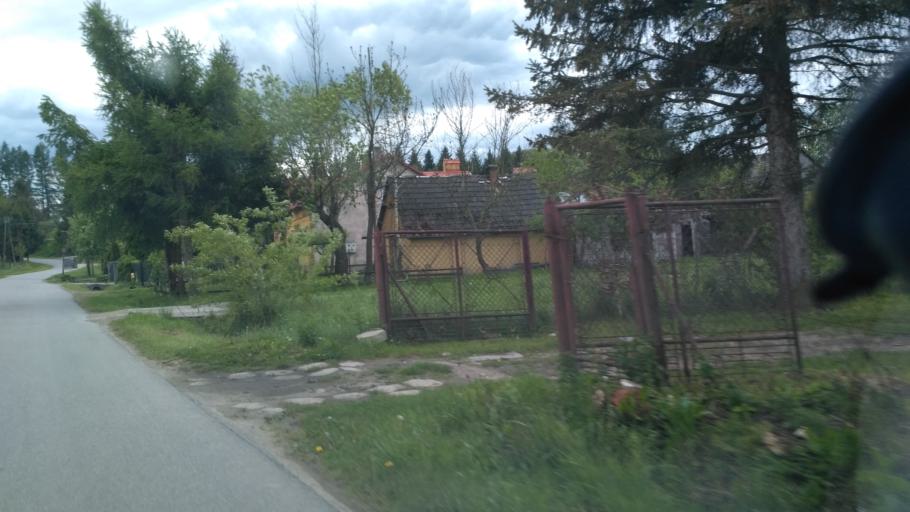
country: PL
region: Subcarpathian Voivodeship
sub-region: Powiat przemyski
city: Przedmiescie Dubieckie
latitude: 49.8303
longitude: 22.3261
